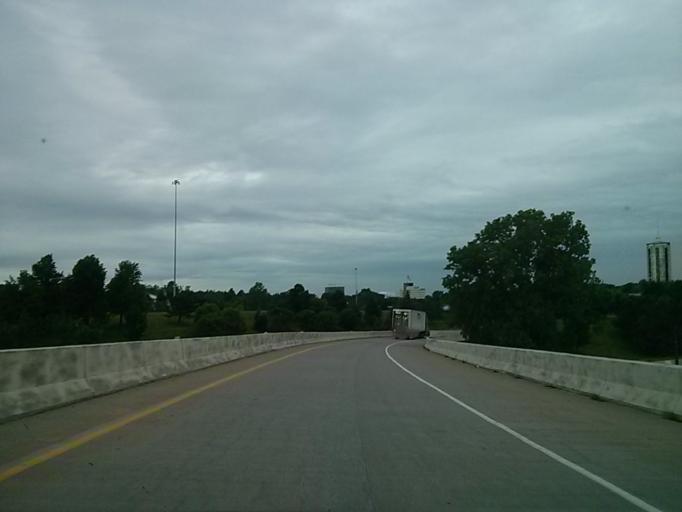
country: US
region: Oklahoma
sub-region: Tulsa County
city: Tulsa
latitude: 36.1440
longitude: -95.9802
